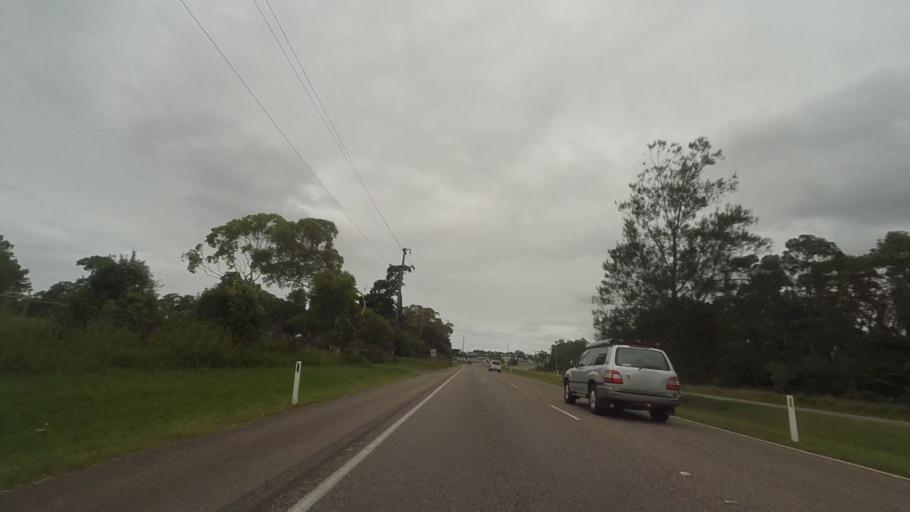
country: AU
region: New South Wales
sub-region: Wyong Shire
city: Buff Point
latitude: -33.1936
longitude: 151.5270
